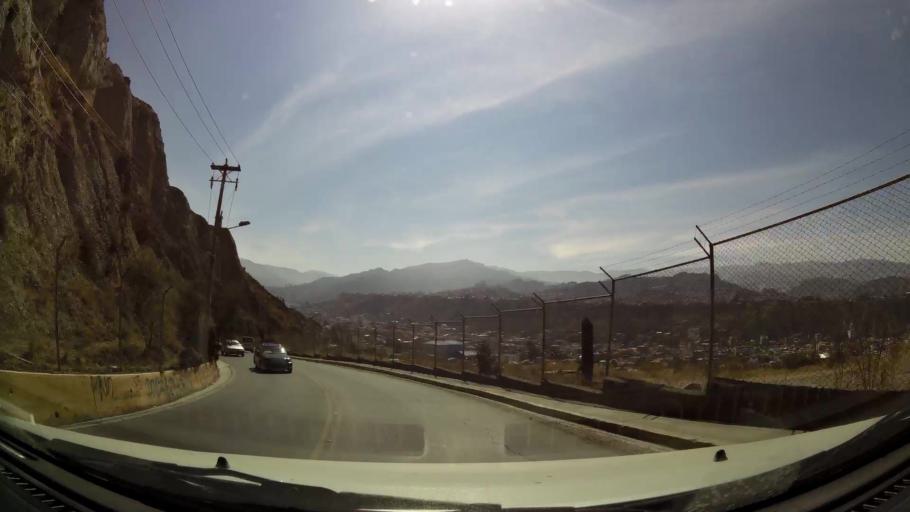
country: BO
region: La Paz
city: La Paz
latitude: -16.5250
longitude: -68.0932
